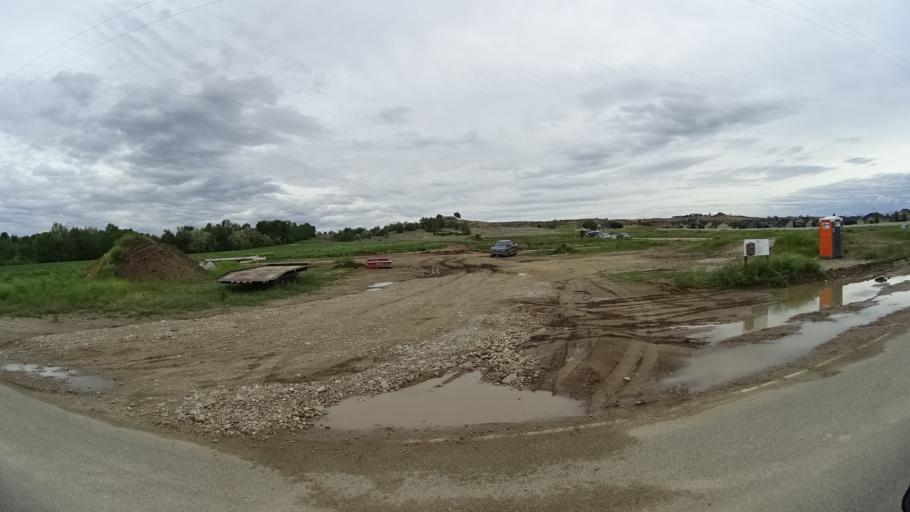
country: US
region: Idaho
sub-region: Ada County
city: Star
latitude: 43.7173
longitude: -116.5011
